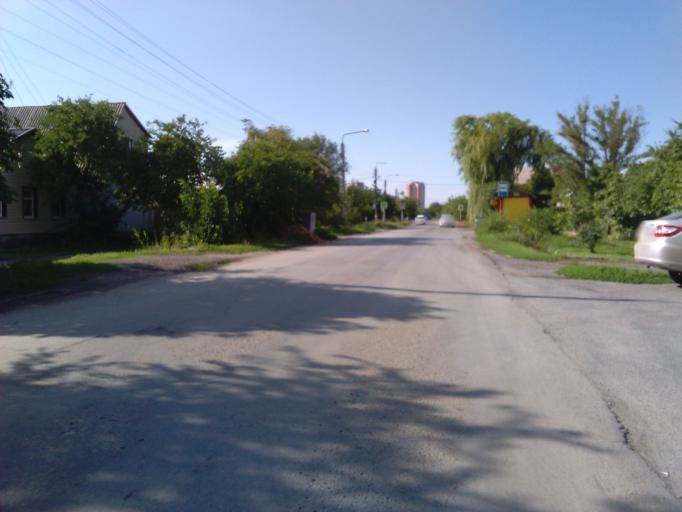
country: RU
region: Rostov
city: Bataysk
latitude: 47.1460
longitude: 39.7350
